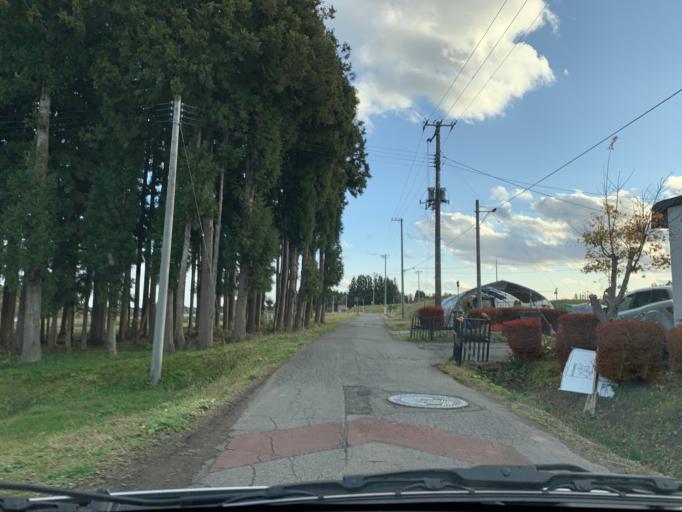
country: JP
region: Iwate
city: Mizusawa
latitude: 39.1118
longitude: 141.0385
